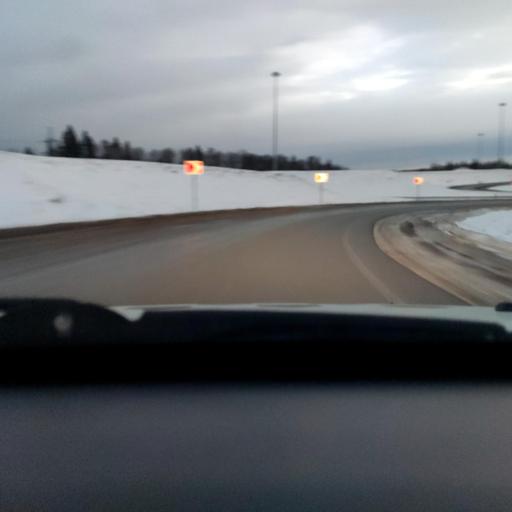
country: RU
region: Perm
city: Novyye Lyady
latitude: 58.0456
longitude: 56.4337
